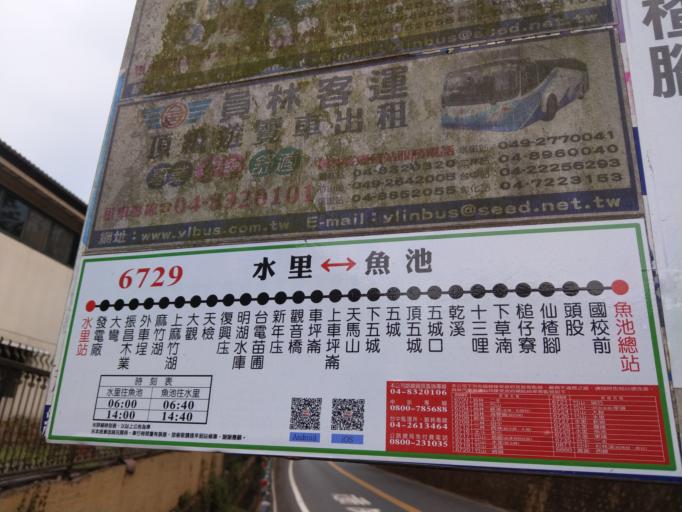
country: TW
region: Taiwan
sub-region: Nantou
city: Puli
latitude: 23.9055
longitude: 120.9134
